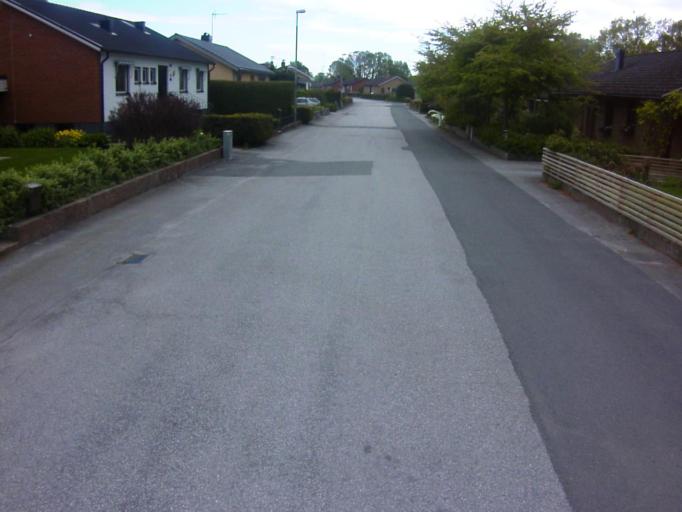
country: SE
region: Blekinge
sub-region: Solvesborgs Kommun
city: Soelvesborg
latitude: 56.0471
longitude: 14.5688
